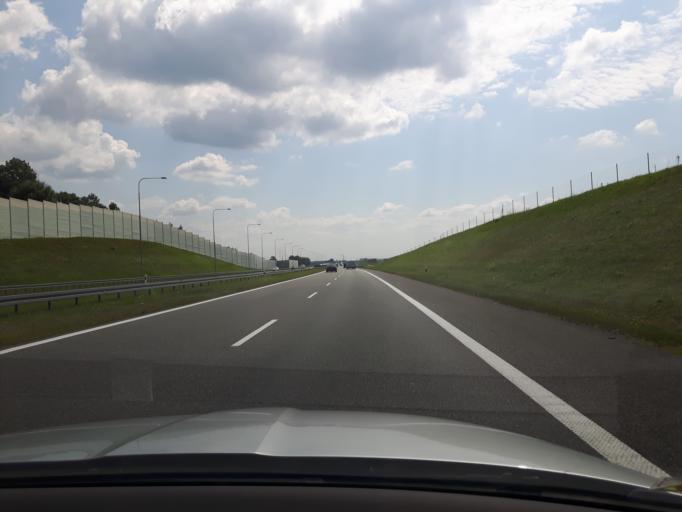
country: PL
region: Warmian-Masurian Voivodeship
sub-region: Powiat ostrodzki
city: Milomlyn
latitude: 53.8118
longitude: 19.7828
